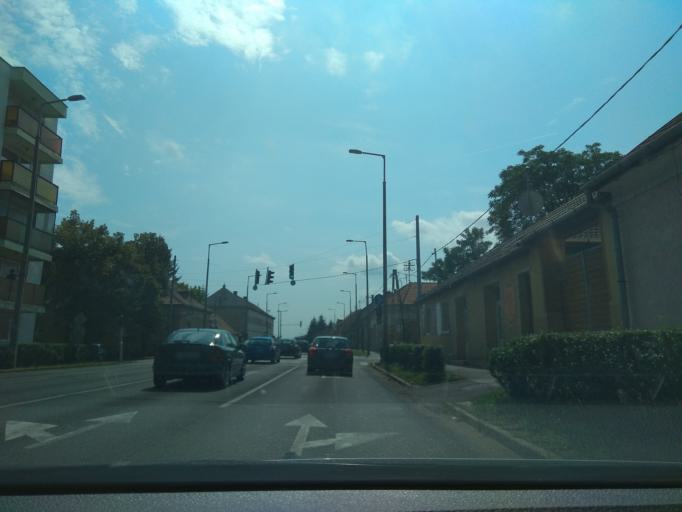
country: HU
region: Heves
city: Eger
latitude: 47.9025
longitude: 20.3666
